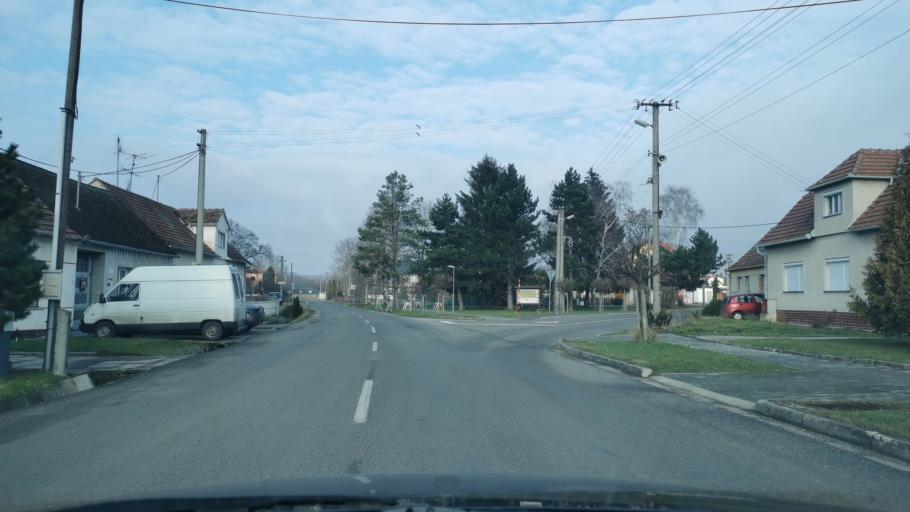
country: SK
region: Trnavsky
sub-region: Okres Senica
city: Senica
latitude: 48.7081
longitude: 17.3378
